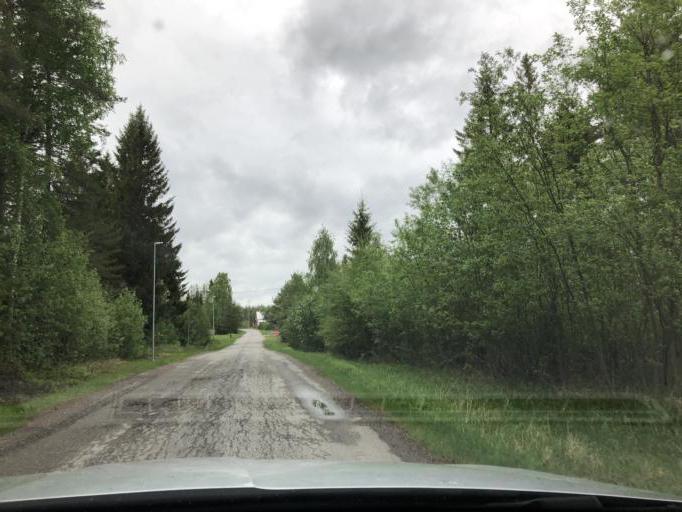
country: SE
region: Norrbotten
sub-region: Pitea Kommun
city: Roknas
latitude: 65.3763
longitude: 21.2792
